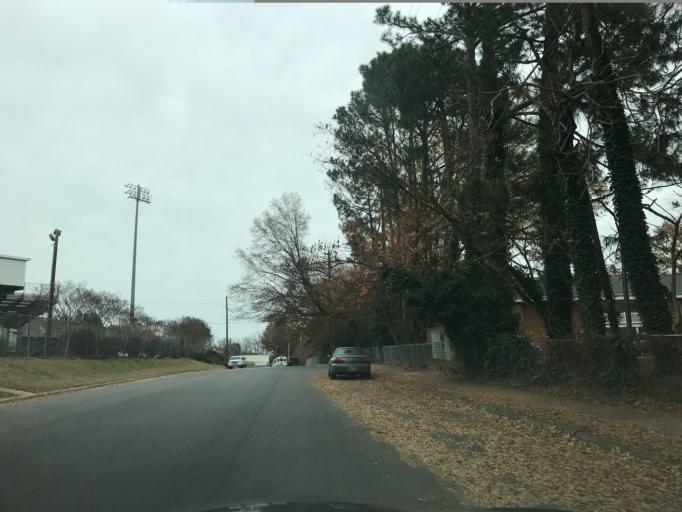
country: US
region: North Carolina
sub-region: Wake County
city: West Raleigh
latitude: 35.7910
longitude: -78.6552
